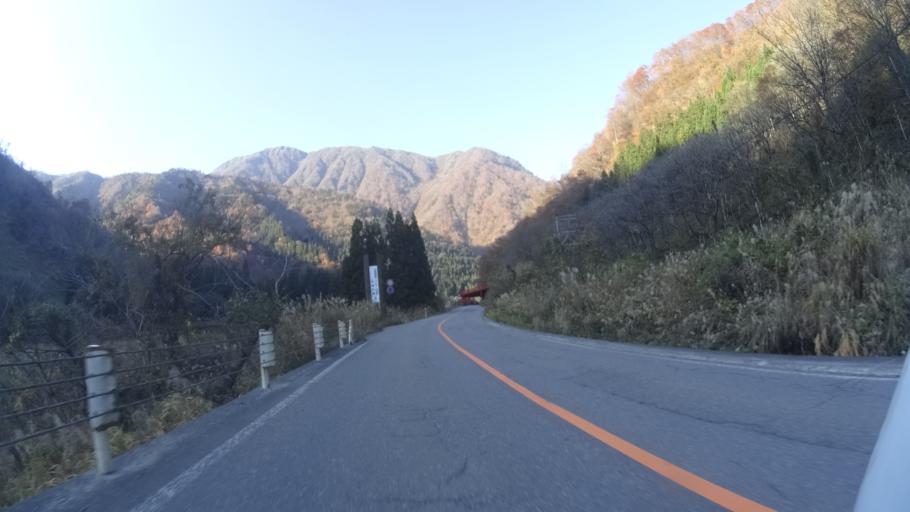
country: JP
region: Fukui
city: Ono
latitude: 35.9144
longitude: 136.6265
